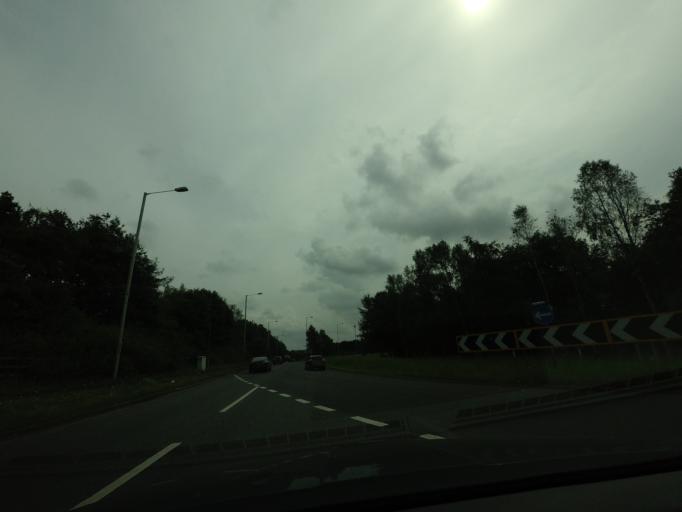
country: GB
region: England
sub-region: Shropshire
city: Tong
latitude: 52.6593
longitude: -2.2995
